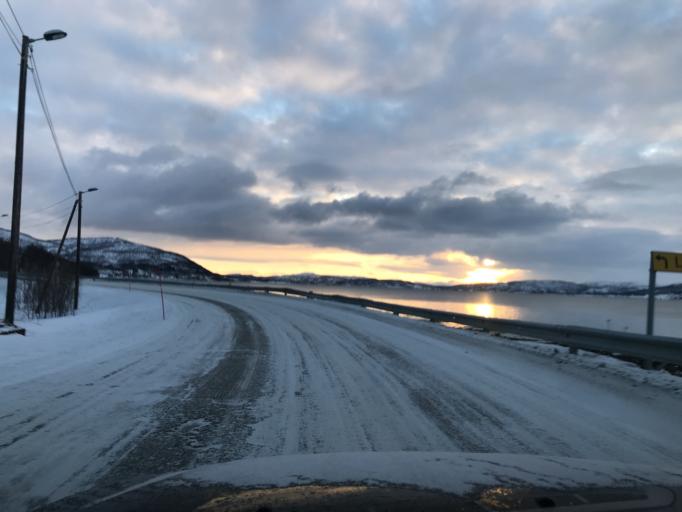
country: NO
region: Troms
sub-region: Lenvik
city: Finnsnes
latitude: 69.3412
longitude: 18.0844
